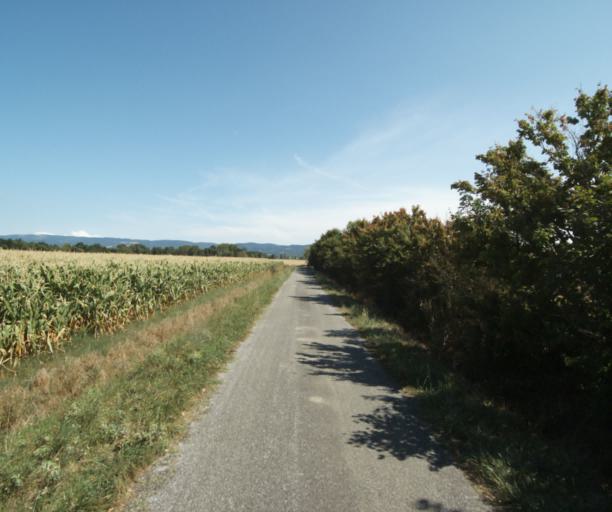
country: FR
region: Midi-Pyrenees
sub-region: Departement de la Haute-Garonne
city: Revel
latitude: 43.4854
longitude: 1.9748
